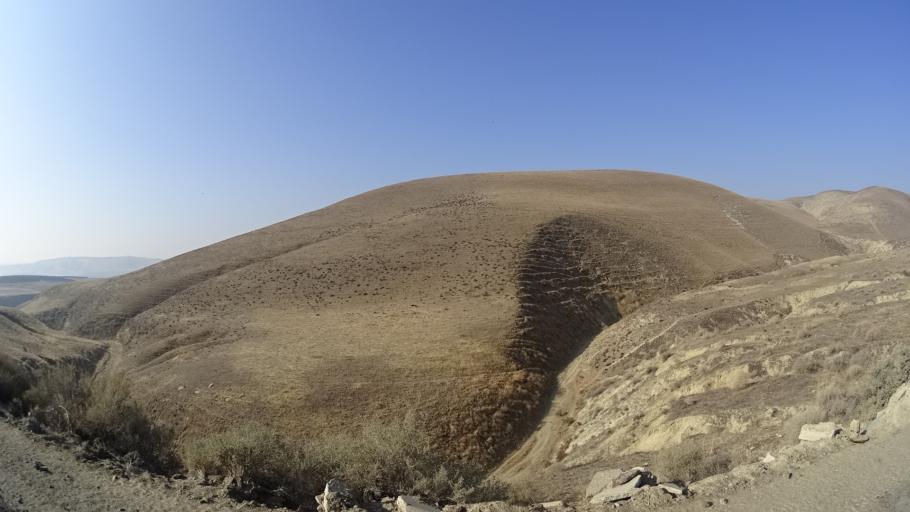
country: US
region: California
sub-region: Kern County
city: Oildale
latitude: 35.4420
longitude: -118.8261
